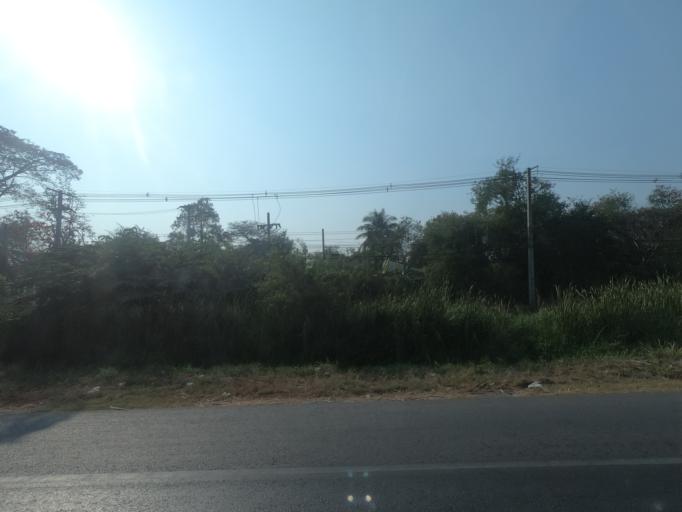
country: TH
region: Khon Kaen
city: Khon Kaen
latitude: 16.3504
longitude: 102.8033
